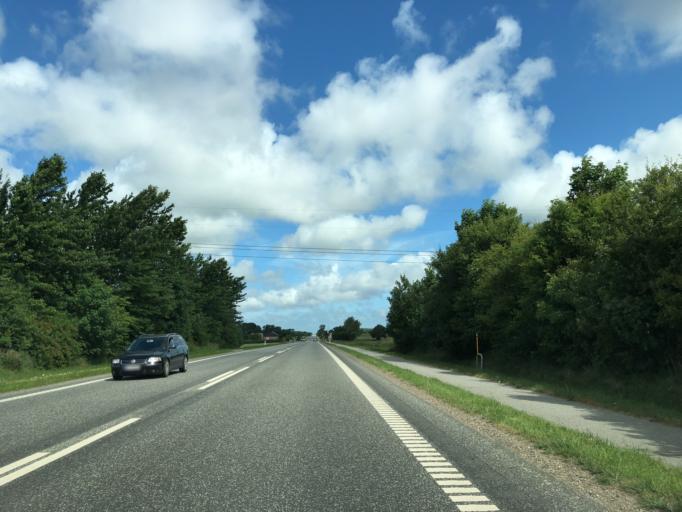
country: DK
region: Central Jutland
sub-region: Holstebro Kommune
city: Holstebro
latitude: 56.4003
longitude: 8.6075
